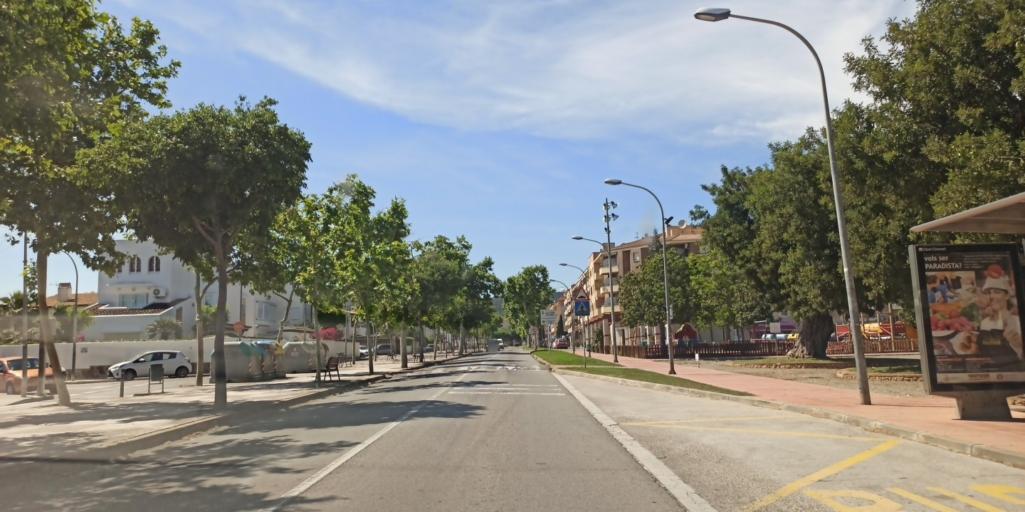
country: ES
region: Catalonia
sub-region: Provincia de Barcelona
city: Sant Pere de Ribes
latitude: 41.2578
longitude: 1.7778
